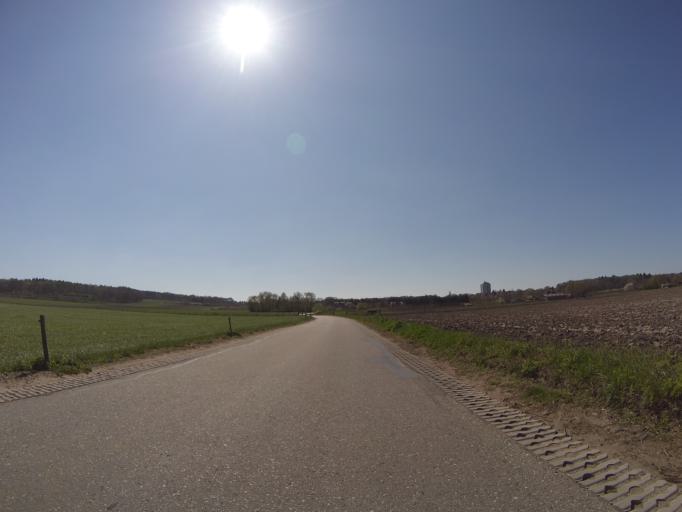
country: NL
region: Utrecht
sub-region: Gemeente Rhenen
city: Rhenen
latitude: 51.9688
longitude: 5.5877
